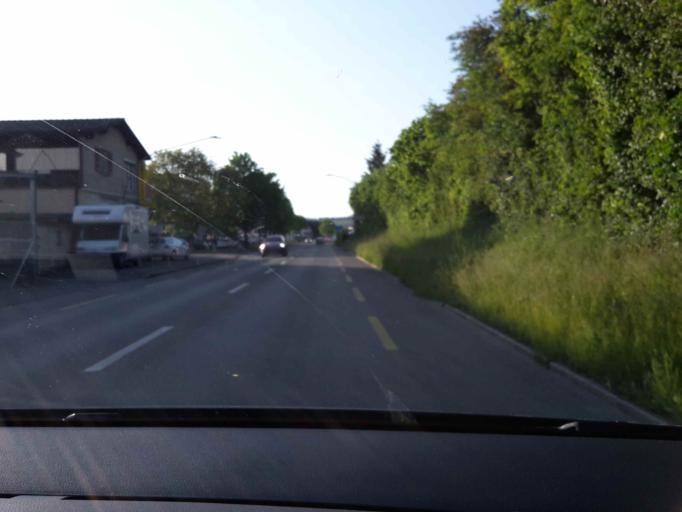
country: CH
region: Bern
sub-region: Thun District
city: Steffisburg
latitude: 46.7778
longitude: 7.6135
